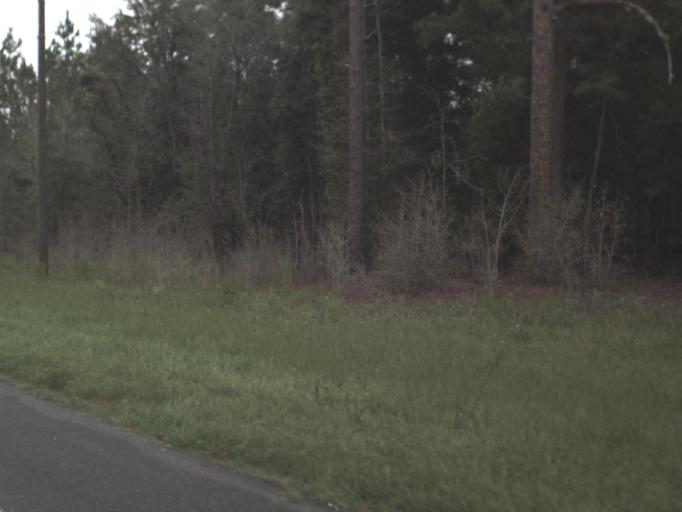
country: US
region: Florida
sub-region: Levy County
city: Williston
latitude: 29.2710
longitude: -82.4426
